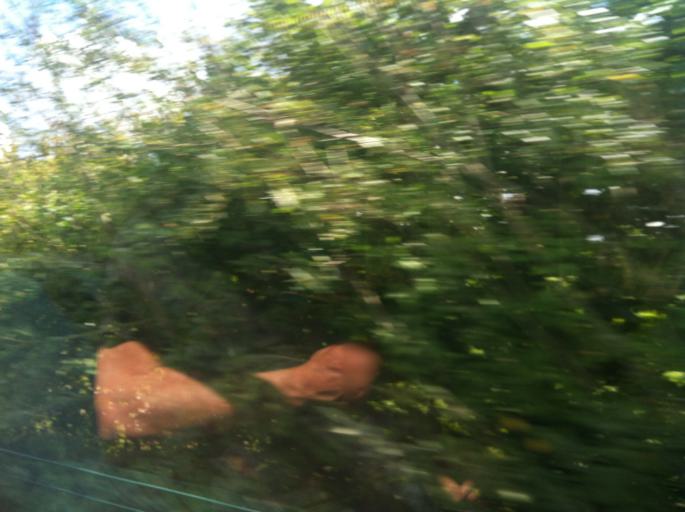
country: DE
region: Bavaria
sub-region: Upper Bavaria
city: Garching bei Munchen
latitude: 48.2330
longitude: 11.6245
